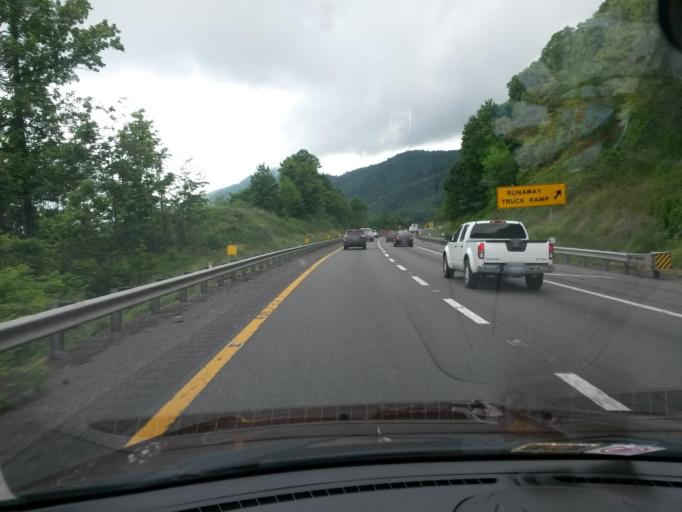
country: US
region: Virginia
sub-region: Carroll County
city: Cana
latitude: 36.6260
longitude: -80.7304
